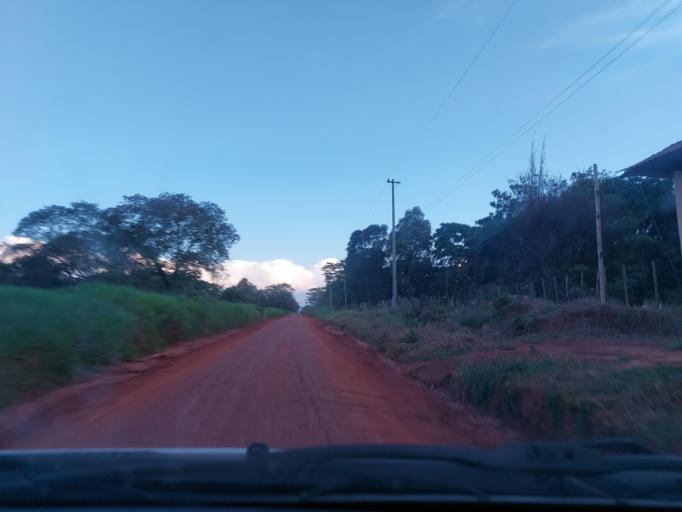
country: PY
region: San Pedro
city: Lima
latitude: -24.1481
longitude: -56.0114
